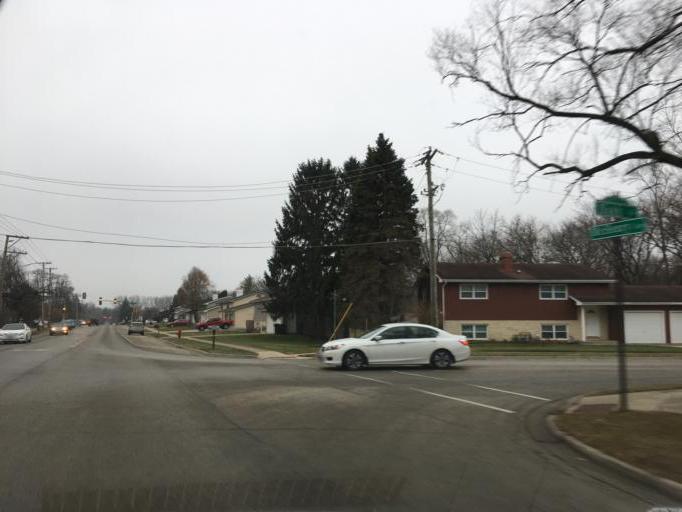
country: US
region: Illinois
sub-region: McHenry County
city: Lakewood
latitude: 42.2230
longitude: -88.3380
